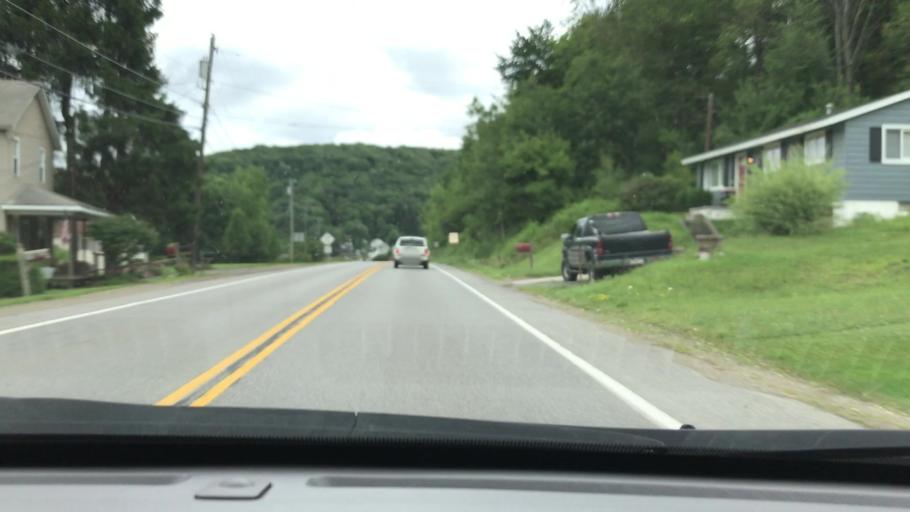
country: US
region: Pennsylvania
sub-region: Elk County
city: Johnsonburg
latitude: 41.4755
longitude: -78.6704
